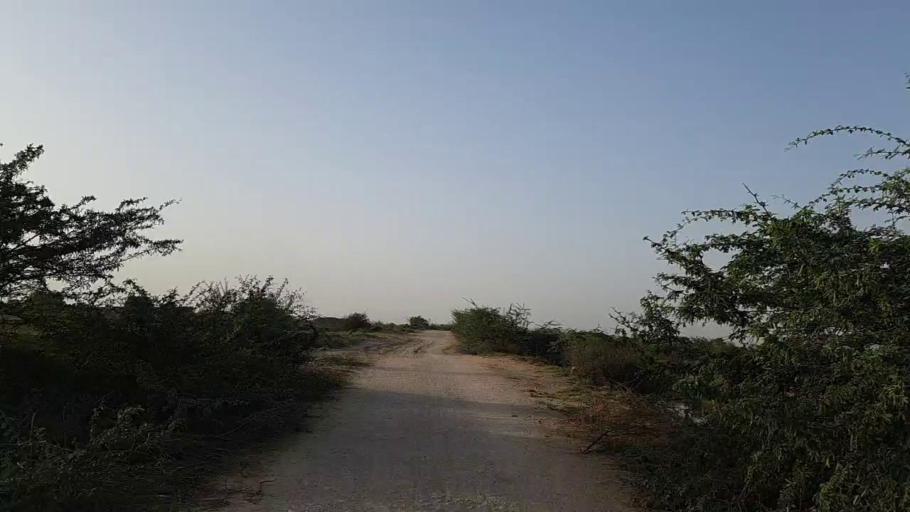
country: PK
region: Sindh
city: Jati
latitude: 24.4018
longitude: 68.1875
